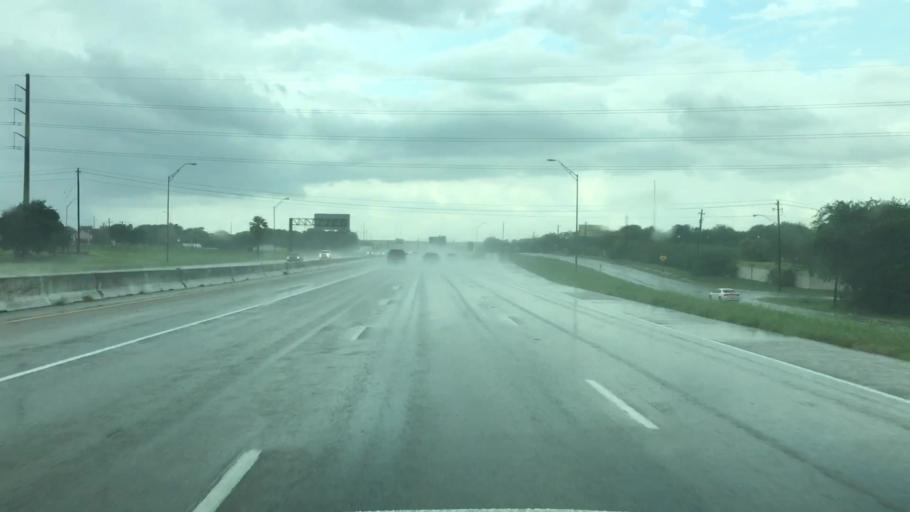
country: US
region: Texas
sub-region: Nueces County
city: Robstown
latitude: 27.8577
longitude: -97.6038
